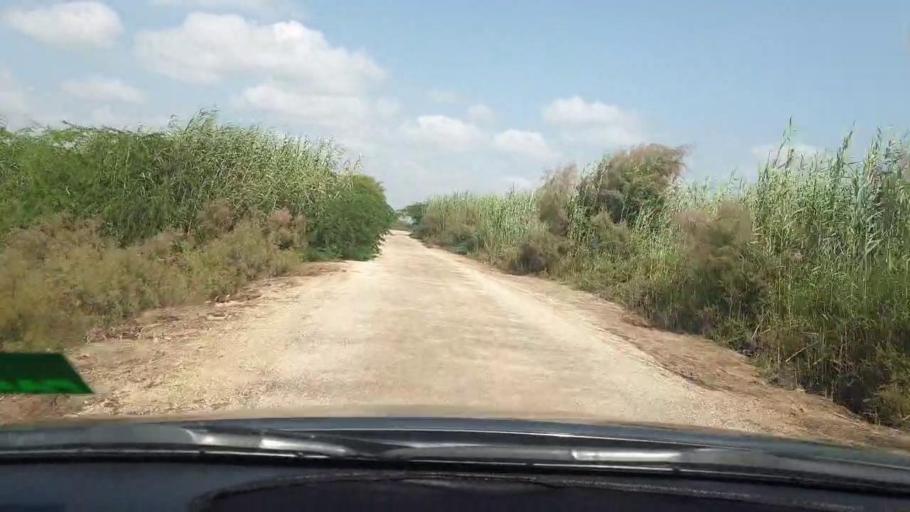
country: PK
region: Sindh
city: Tando Bago
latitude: 24.8508
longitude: 69.0347
